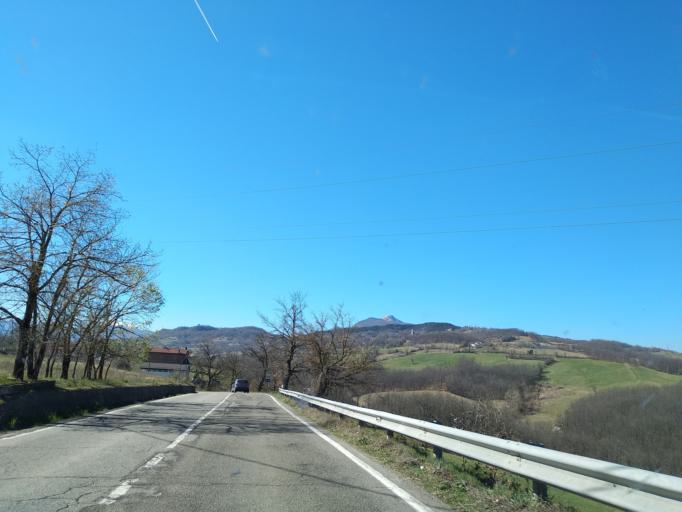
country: IT
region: Emilia-Romagna
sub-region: Provincia di Reggio Emilia
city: Castelnovo ne'Monti
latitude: 44.4267
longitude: 10.3822
